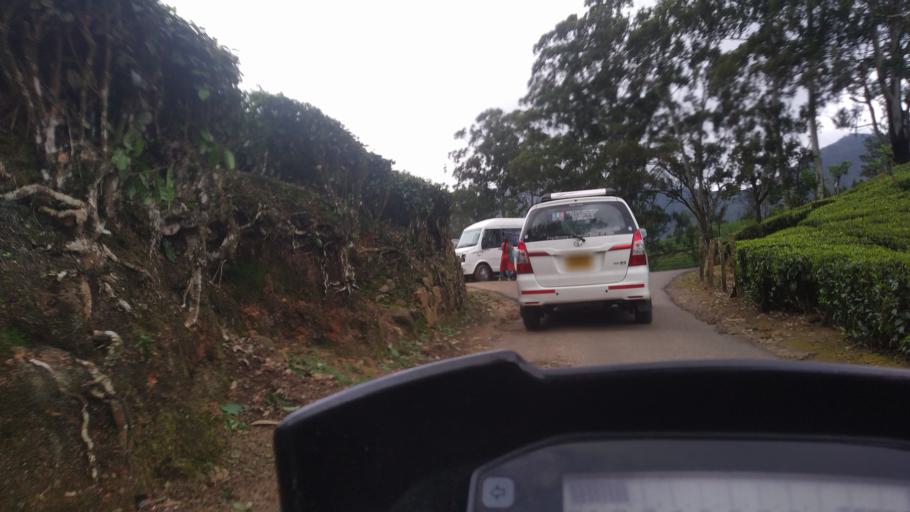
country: IN
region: Kerala
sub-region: Idukki
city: Munnar
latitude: 10.0628
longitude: 77.1070
